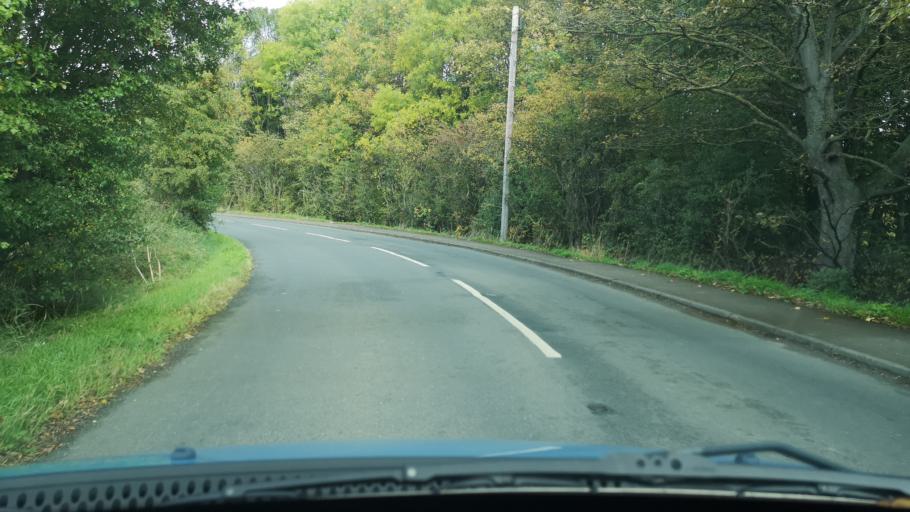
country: GB
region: England
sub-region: City and Borough of Wakefield
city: Featherstone
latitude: 53.6862
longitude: -1.3856
